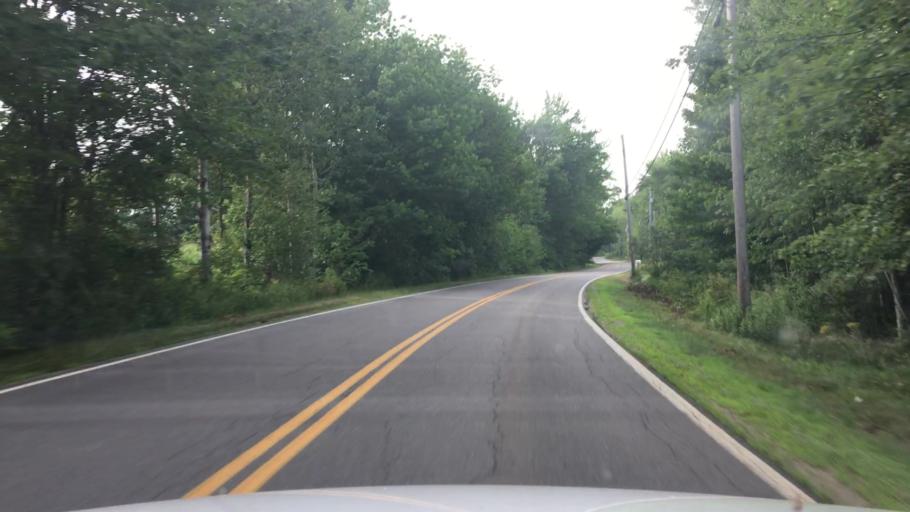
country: US
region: Maine
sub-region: Lincoln County
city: Waldoboro
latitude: 44.1423
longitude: -69.3726
